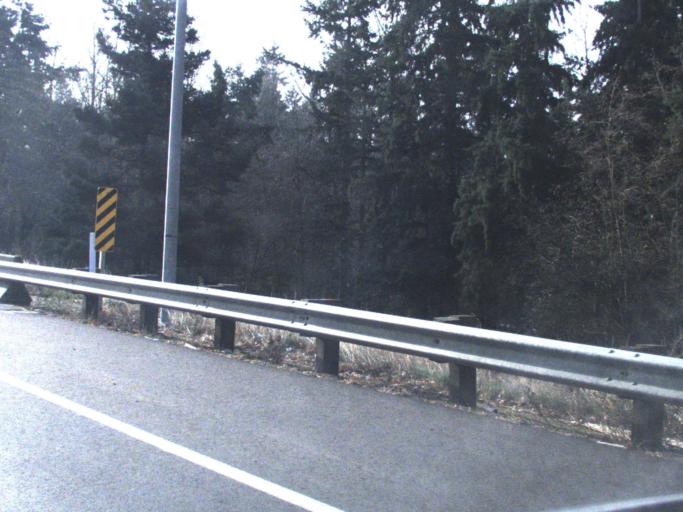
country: US
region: Washington
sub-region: King County
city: Lakeland North
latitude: 47.3527
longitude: -122.2962
